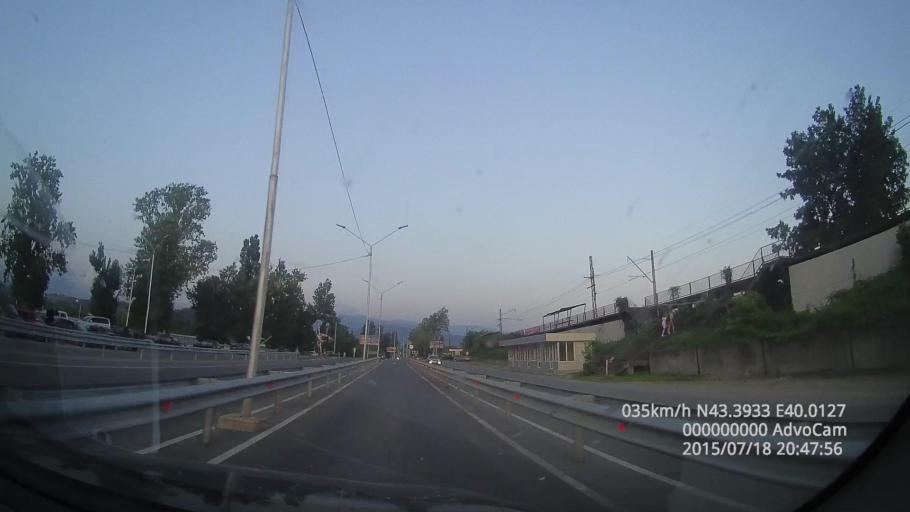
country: GE
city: Gantiadi
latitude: 43.3932
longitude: 40.0135
